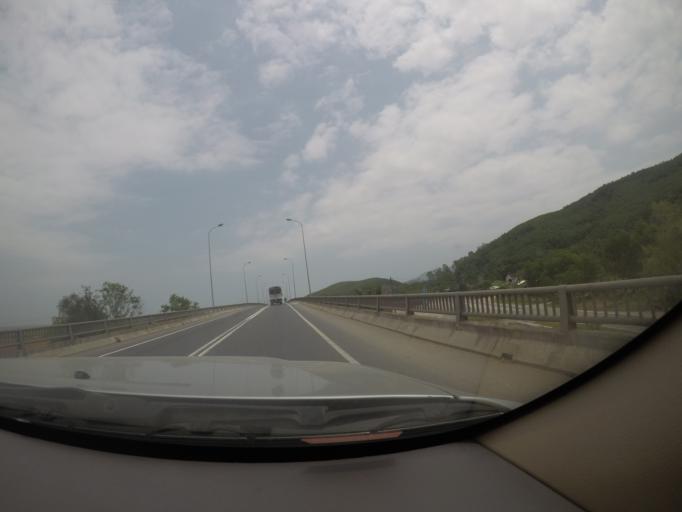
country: VN
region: Thua Thien-Hue
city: Phu Loc
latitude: 16.2733
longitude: 107.8981
